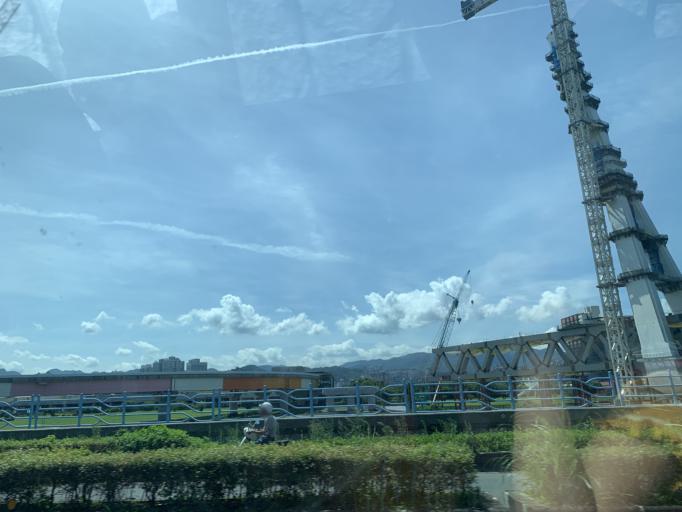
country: TW
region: Taipei
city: Taipei
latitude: 24.9868
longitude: 121.5242
